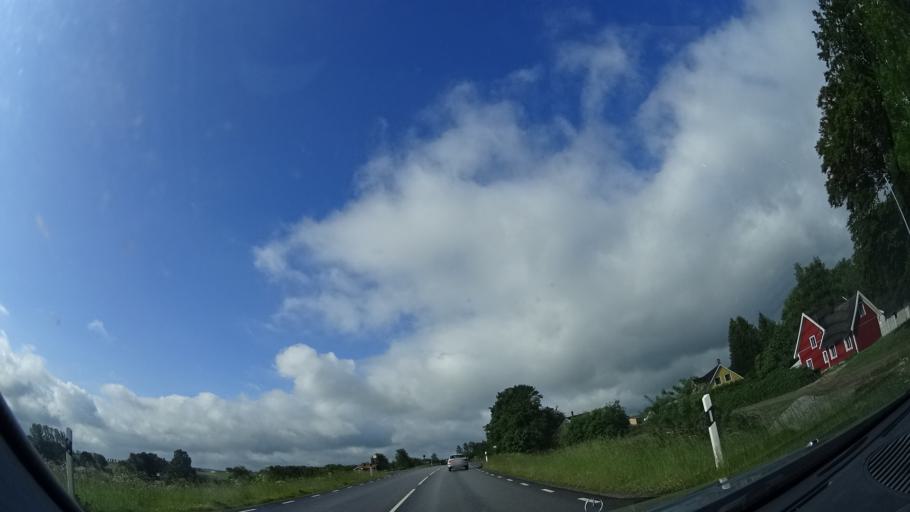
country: SE
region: Skane
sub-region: Eslovs Kommun
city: Stehag
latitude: 55.9255
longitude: 13.3758
